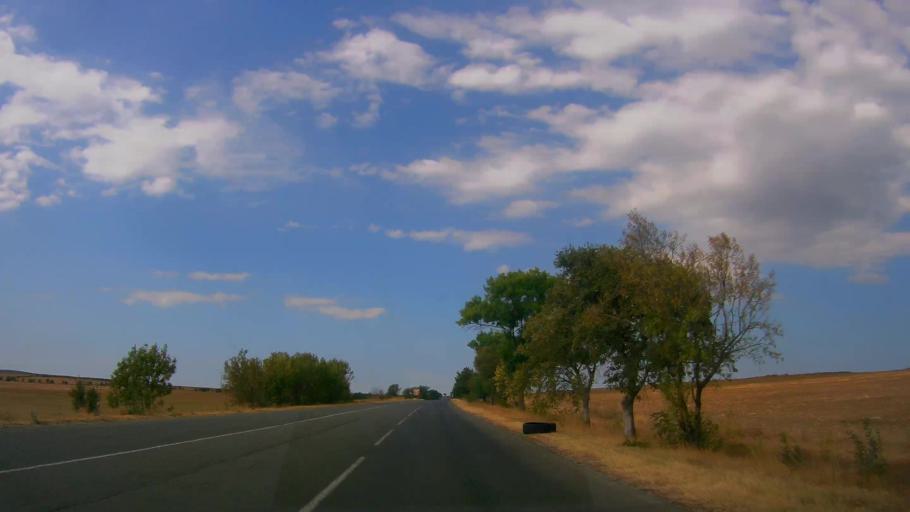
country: BG
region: Burgas
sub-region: Obshtina Aytos
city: Aytos
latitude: 42.6969
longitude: 27.1981
